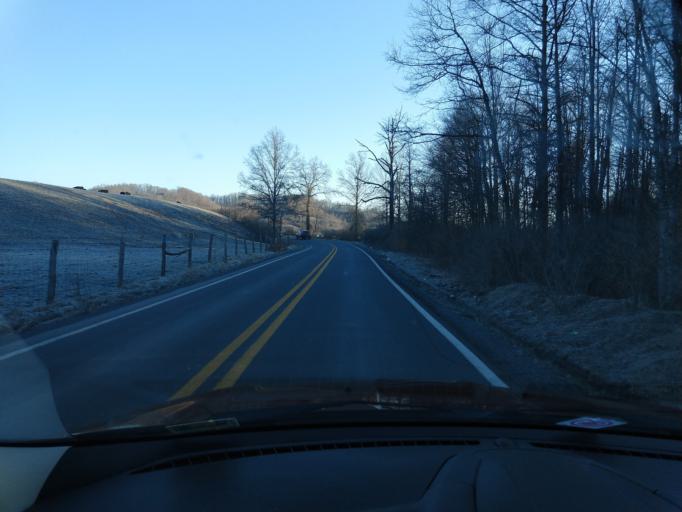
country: US
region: West Virginia
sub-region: Greenbrier County
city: Rainelle
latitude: 37.8623
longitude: -80.7192
